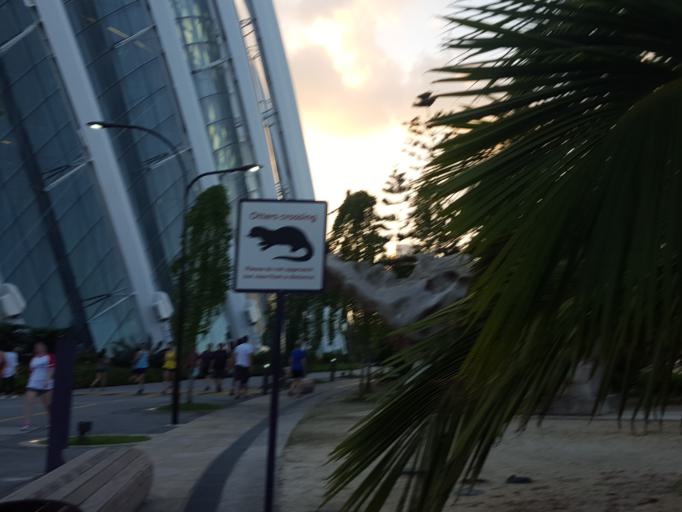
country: SG
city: Singapore
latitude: 1.2839
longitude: 103.8669
